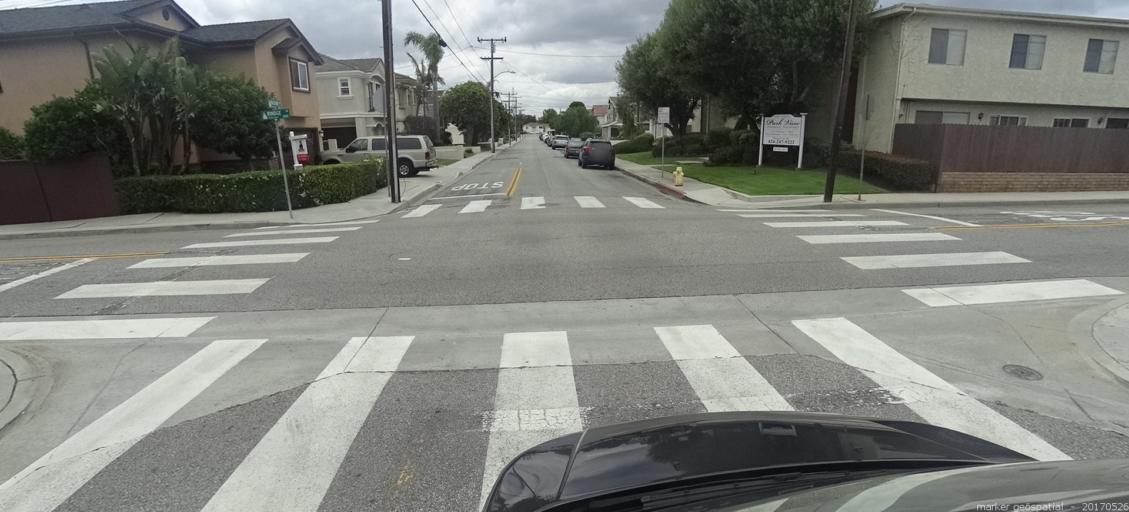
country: US
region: California
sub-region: Los Angeles County
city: Lawndale
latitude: 33.8847
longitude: -118.3730
